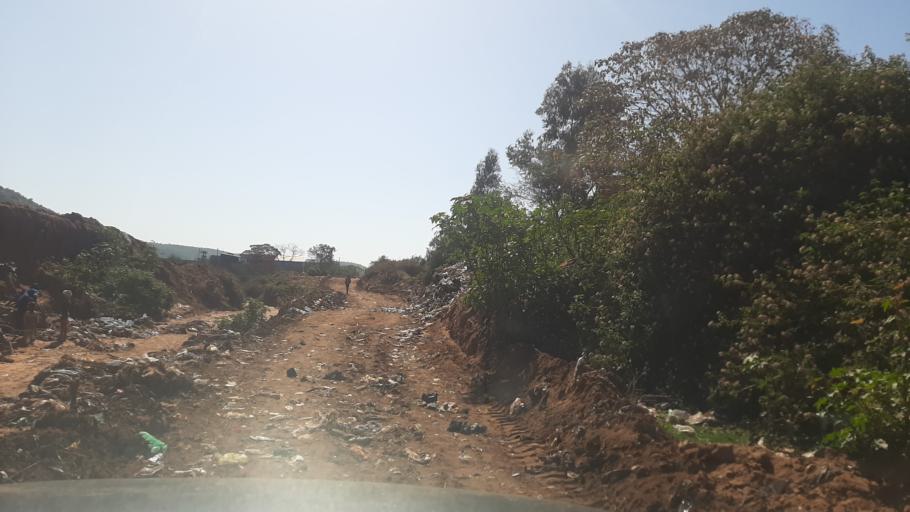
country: ET
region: Oromiya
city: Yabelo
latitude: 4.8940
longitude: 38.1003
